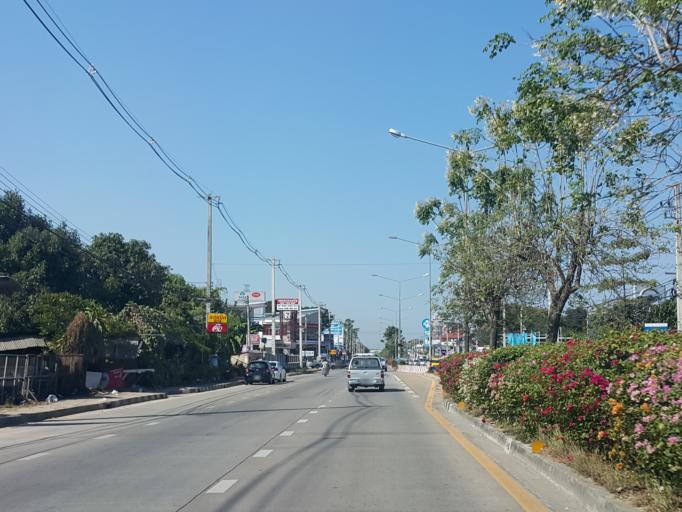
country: TH
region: Chiang Mai
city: San Sai
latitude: 18.8155
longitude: 99.0213
